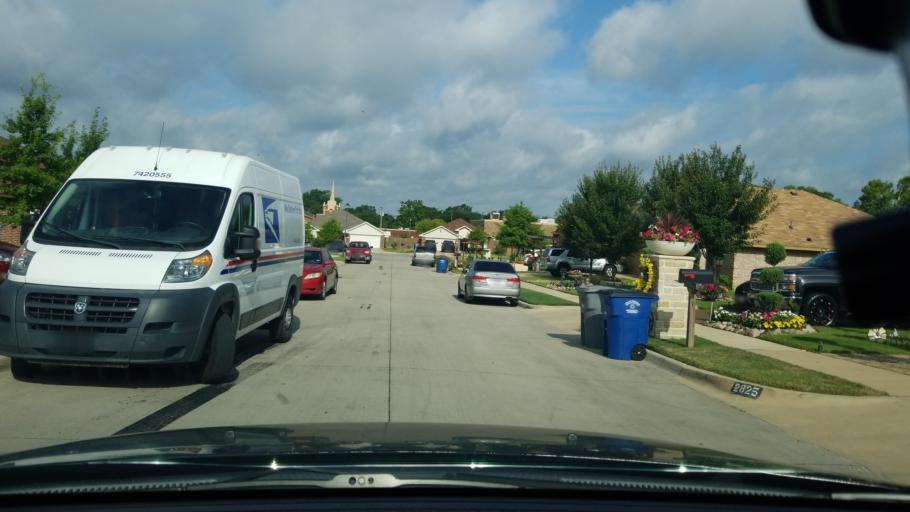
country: US
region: Texas
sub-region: Dallas County
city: Mesquite
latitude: 32.8181
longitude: -96.6657
